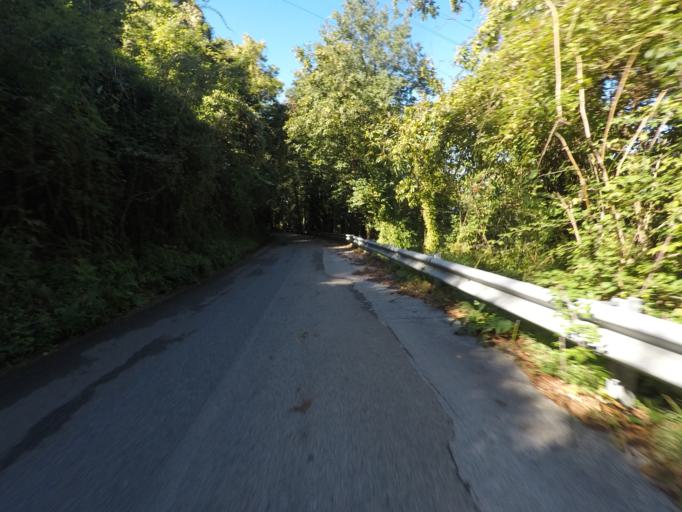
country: IT
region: Tuscany
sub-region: Provincia di Massa-Carrara
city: Montignoso
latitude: 44.0377
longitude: 10.1602
